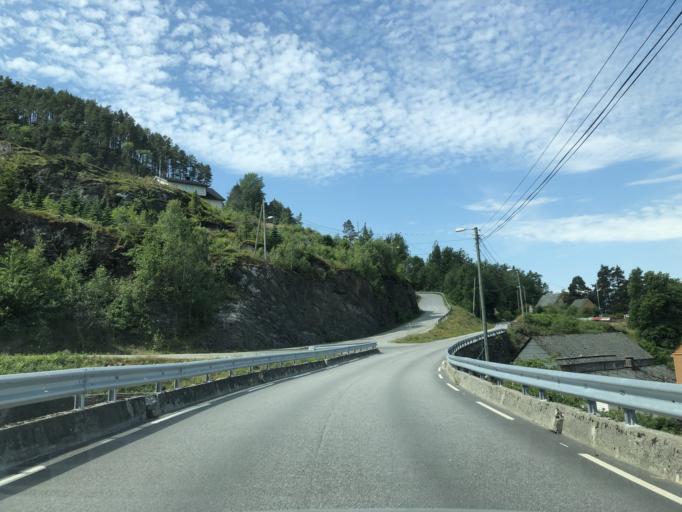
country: NO
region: Hordaland
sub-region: Jondal
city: Jondal
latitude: 60.3036
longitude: 6.2835
